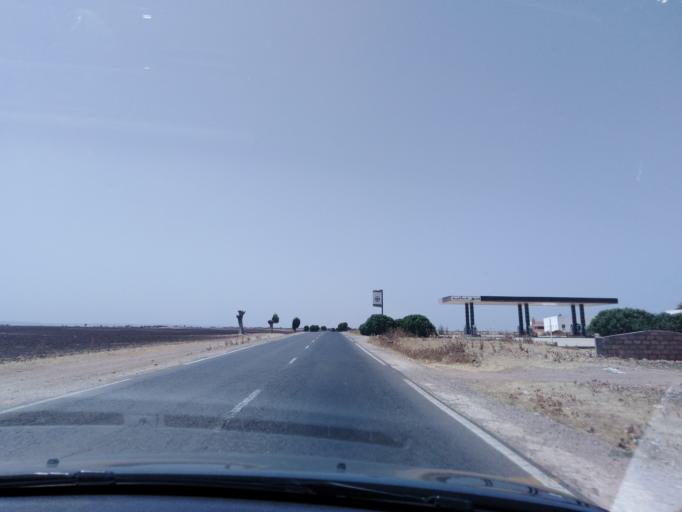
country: MA
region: Doukkala-Abda
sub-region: Safi
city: Youssoufia
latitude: 32.3929
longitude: -8.8214
